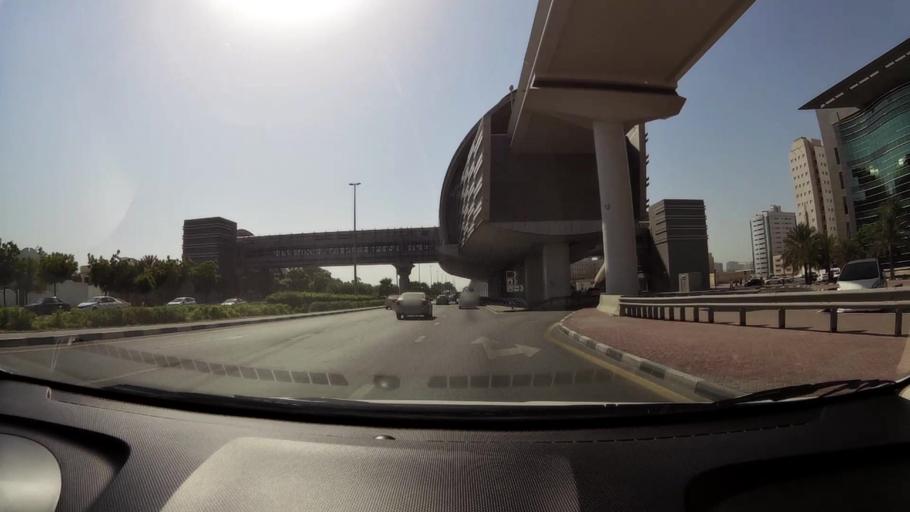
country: AE
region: Ash Shariqah
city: Sharjah
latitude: 25.2726
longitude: 55.3701
